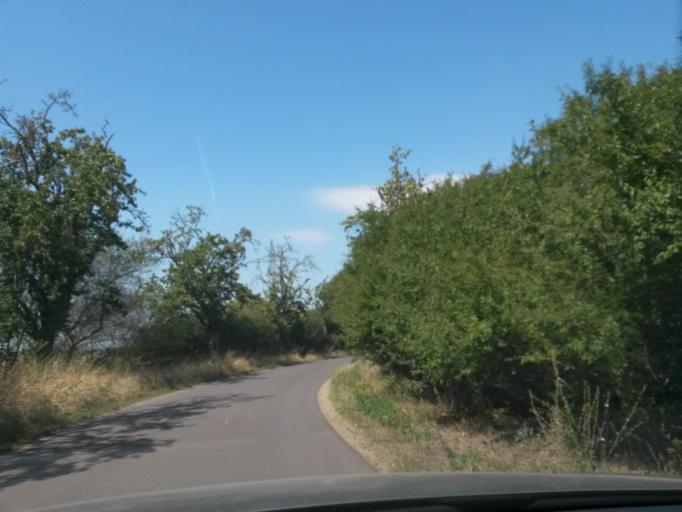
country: DE
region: Saxony-Anhalt
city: Jerichow
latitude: 52.3953
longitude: 11.9868
